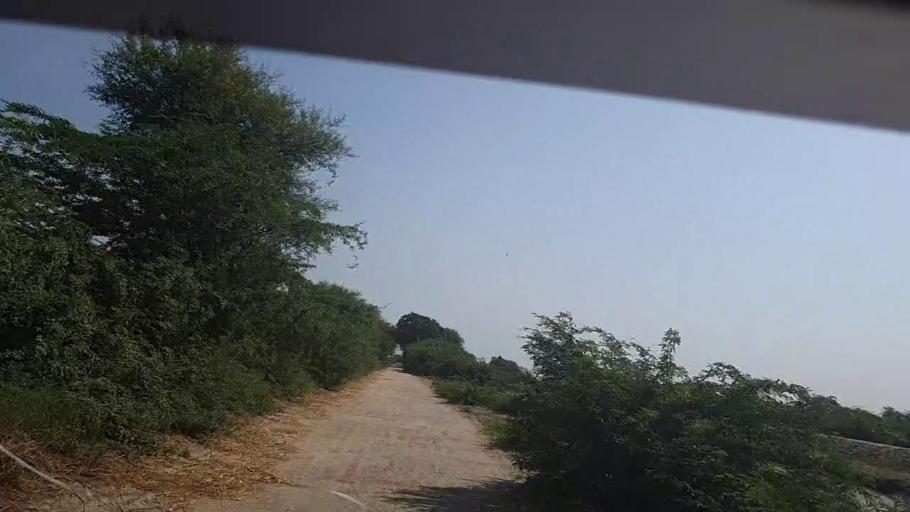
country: PK
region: Sindh
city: Rajo Khanani
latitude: 24.9841
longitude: 68.8648
